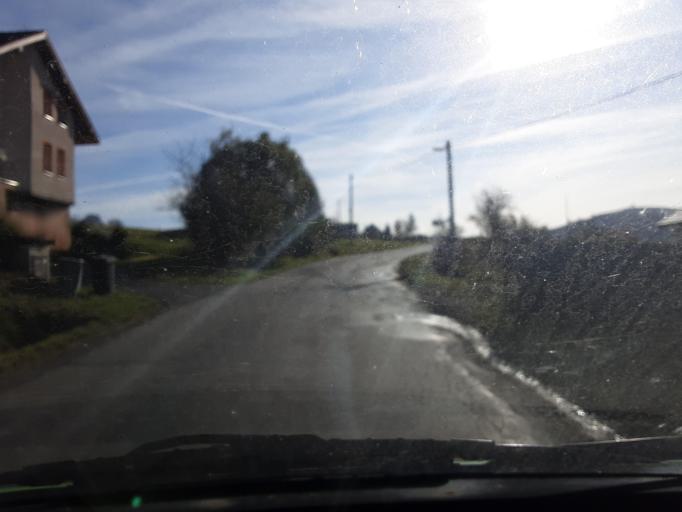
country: CZ
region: Plzensky
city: Janovice nad Uhlavou
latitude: 49.3769
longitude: 13.1682
